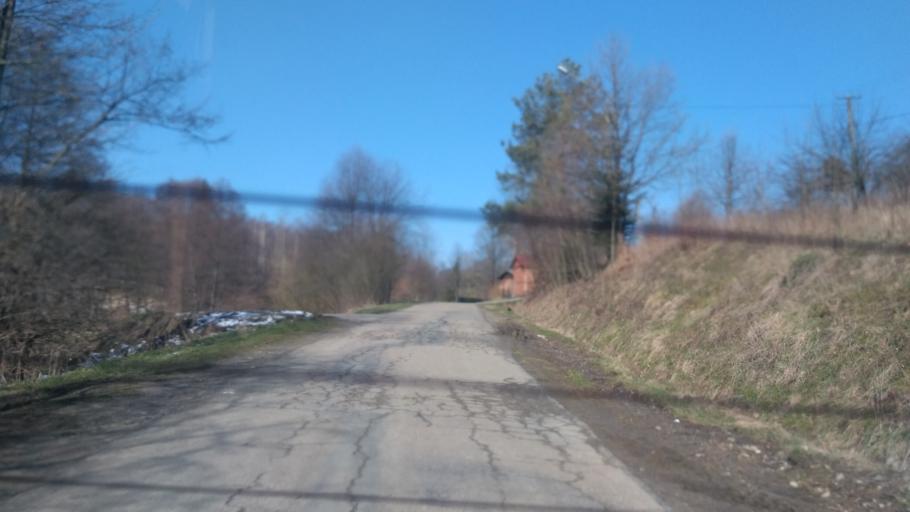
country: PL
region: Subcarpathian Voivodeship
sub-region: Powiat strzyzowski
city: Gwoznica Gorna
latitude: 49.8180
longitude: 22.0201
